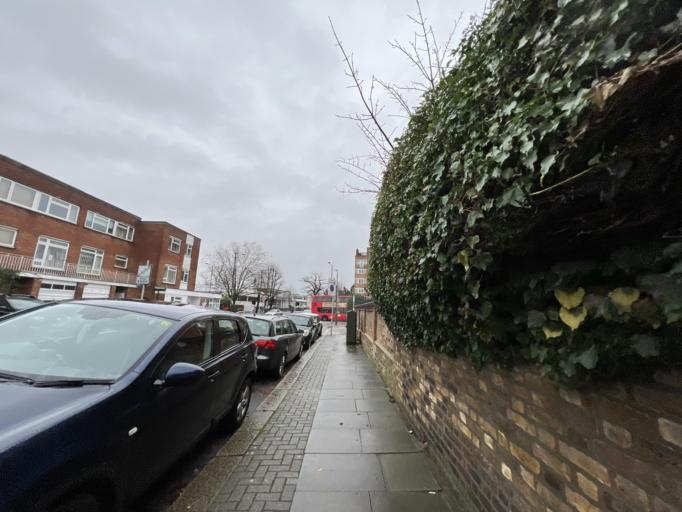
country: GB
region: England
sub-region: Greater London
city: Wandsworth
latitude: 51.4627
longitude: -0.2282
